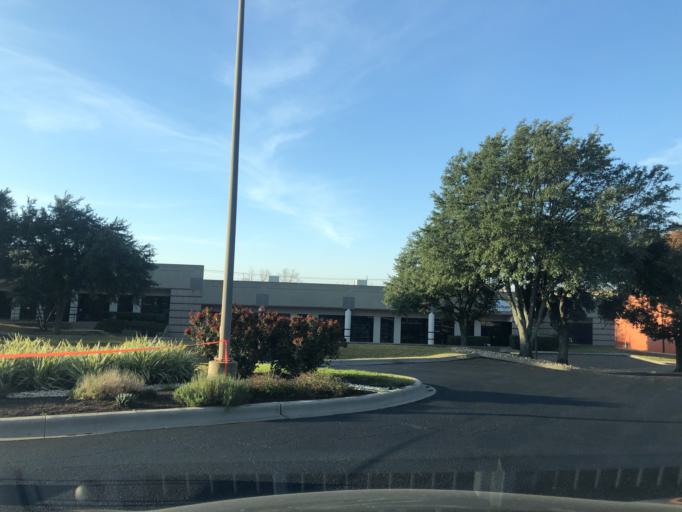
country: US
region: Texas
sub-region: Travis County
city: Wells Branch
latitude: 30.4361
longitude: -97.6855
